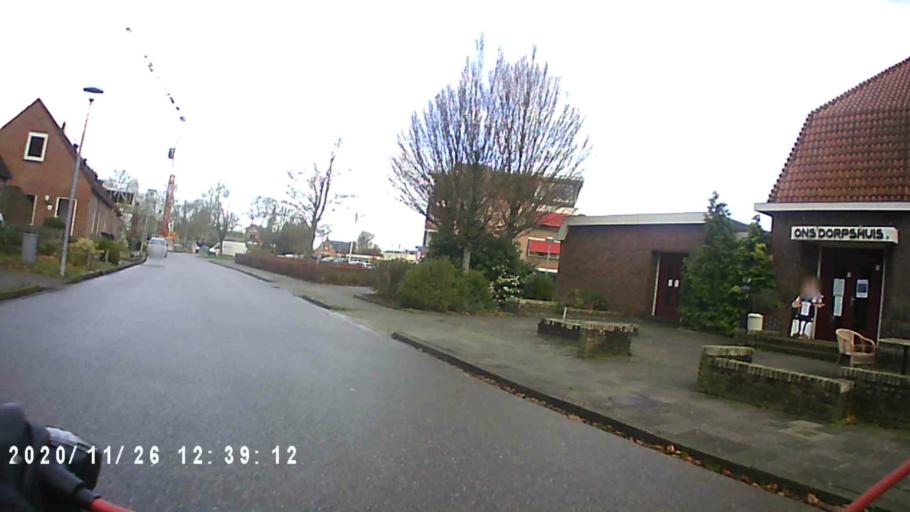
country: NL
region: Groningen
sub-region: Gemeente Appingedam
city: Appingedam
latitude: 53.3324
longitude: 6.7488
